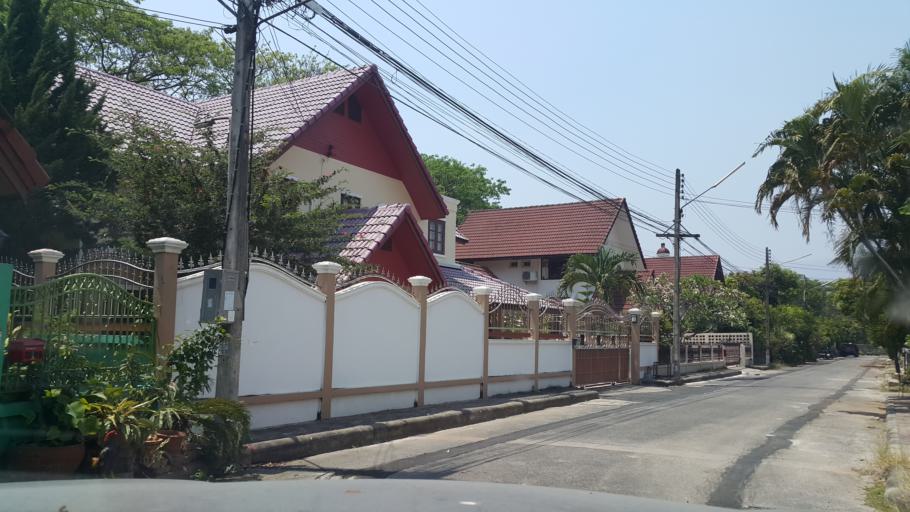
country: TH
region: Chiang Mai
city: Chiang Mai
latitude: 18.7566
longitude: 98.9905
